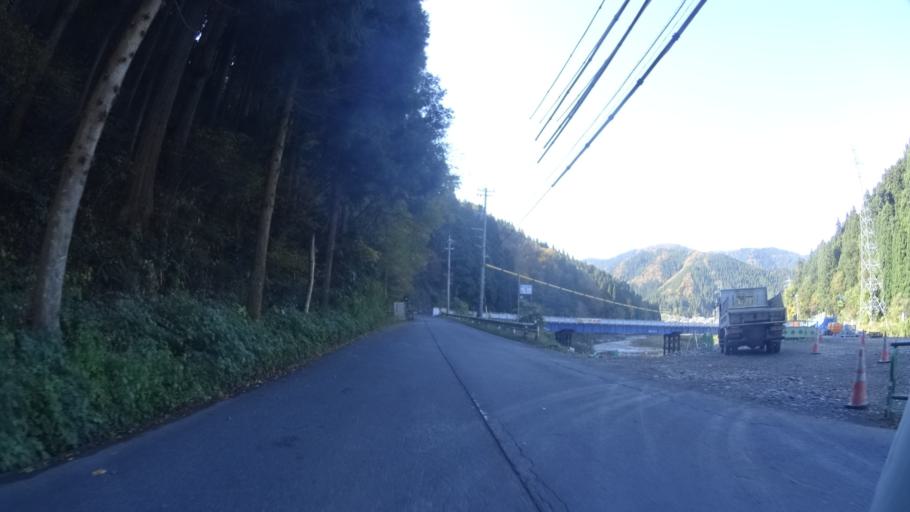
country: JP
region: Fukui
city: Ono
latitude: 35.9833
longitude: 136.3674
